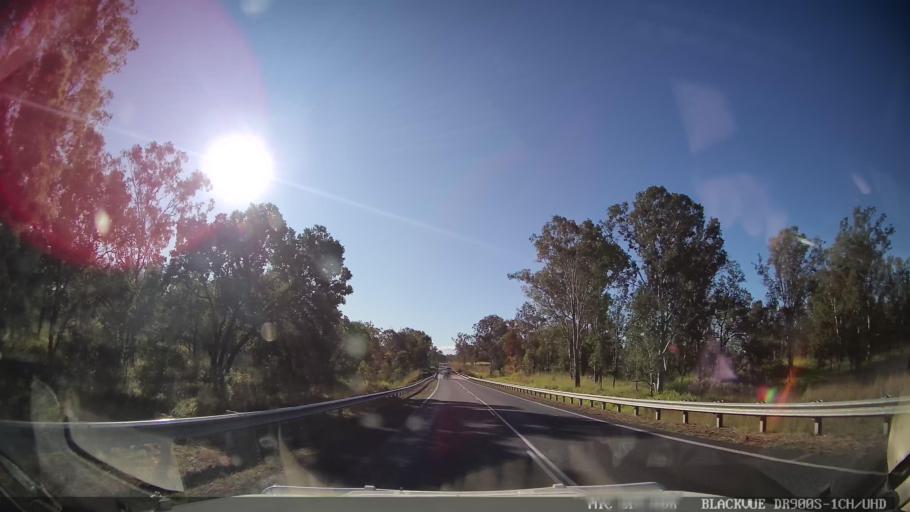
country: AU
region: Queensland
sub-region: Bundaberg
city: Sharon
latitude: -24.8294
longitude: 151.7084
